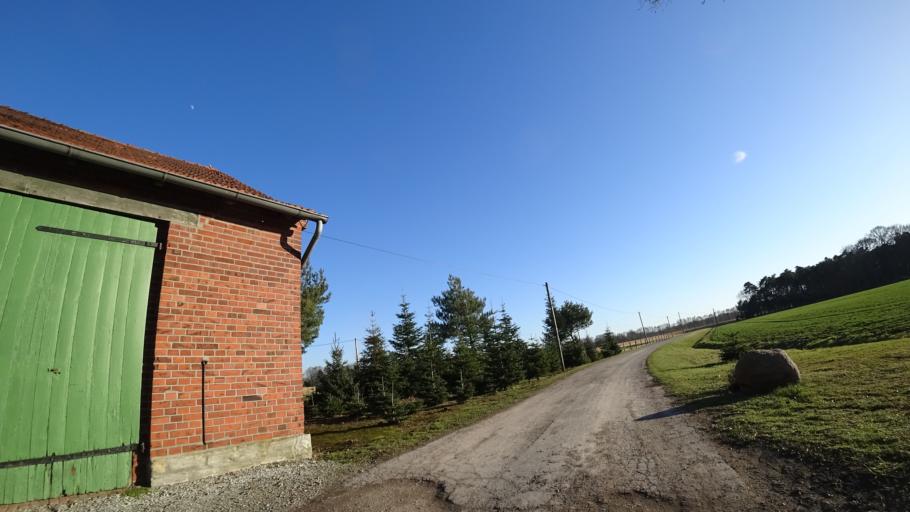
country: DE
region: North Rhine-Westphalia
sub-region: Regierungsbezirk Detmold
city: Guetersloh
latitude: 51.9301
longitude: 8.3300
